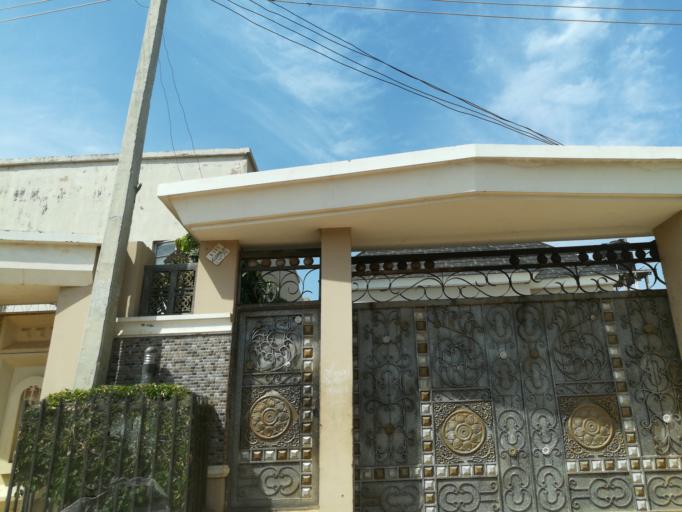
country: NG
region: Kano
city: Kano
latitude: 12.0151
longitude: 8.5086
